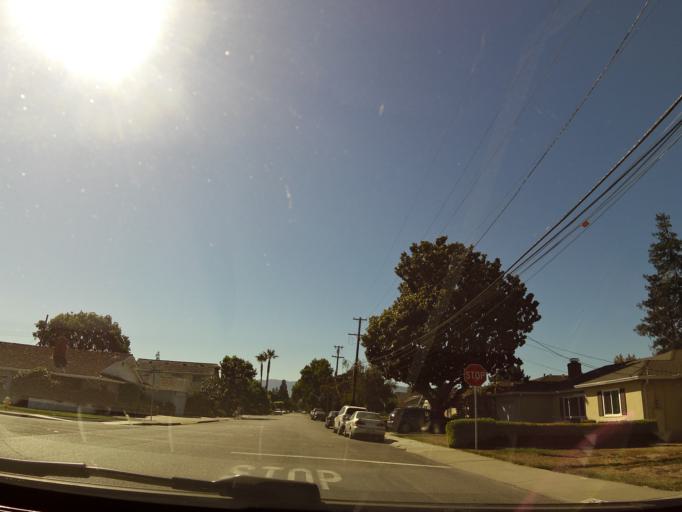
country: US
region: California
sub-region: Santa Clara County
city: Buena Vista
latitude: 37.2929
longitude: -121.9181
